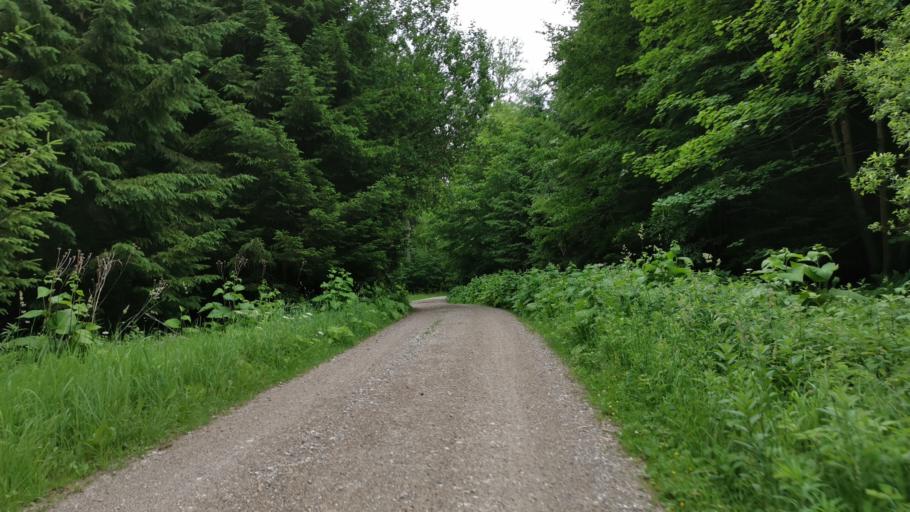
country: DE
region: Bavaria
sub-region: Upper Bavaria
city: Schaftlarn
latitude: 48.0097
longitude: 11.4365
